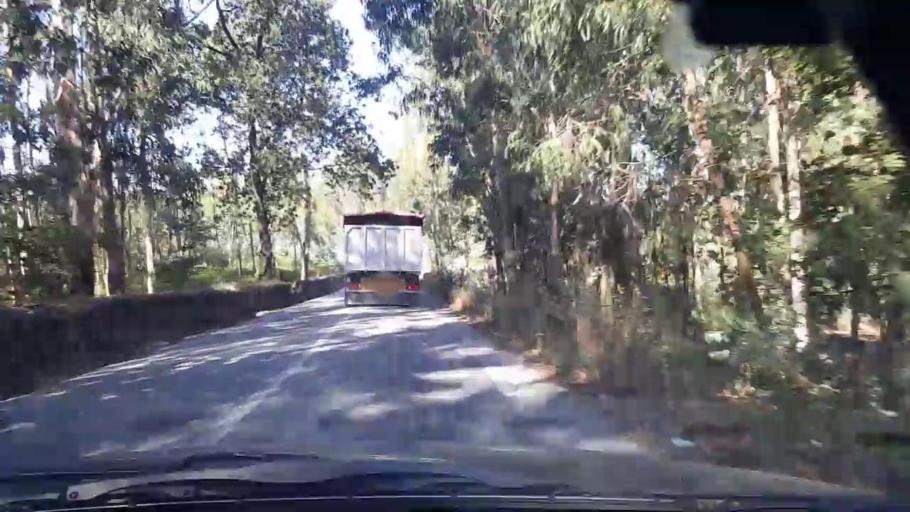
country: PT
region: Braga
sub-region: Vila Nova de Famalicao
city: Ribeirao
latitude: 41.3631
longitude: -8.6232
